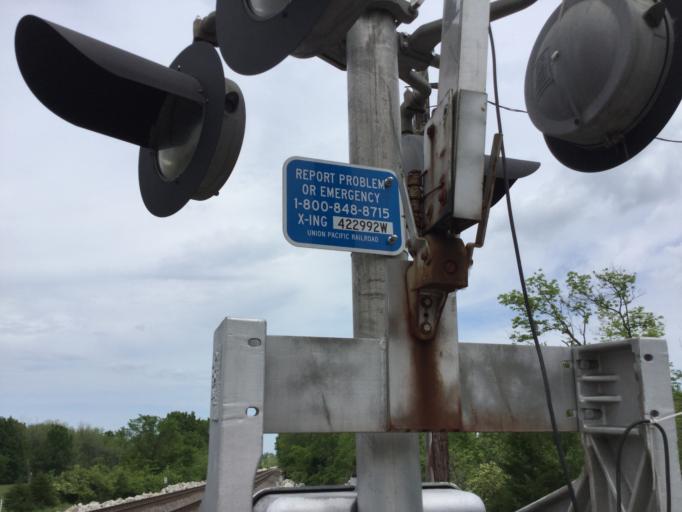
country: US
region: Missouri
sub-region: Jackson County
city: Grandview
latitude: 38.8549
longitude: -94.6141
